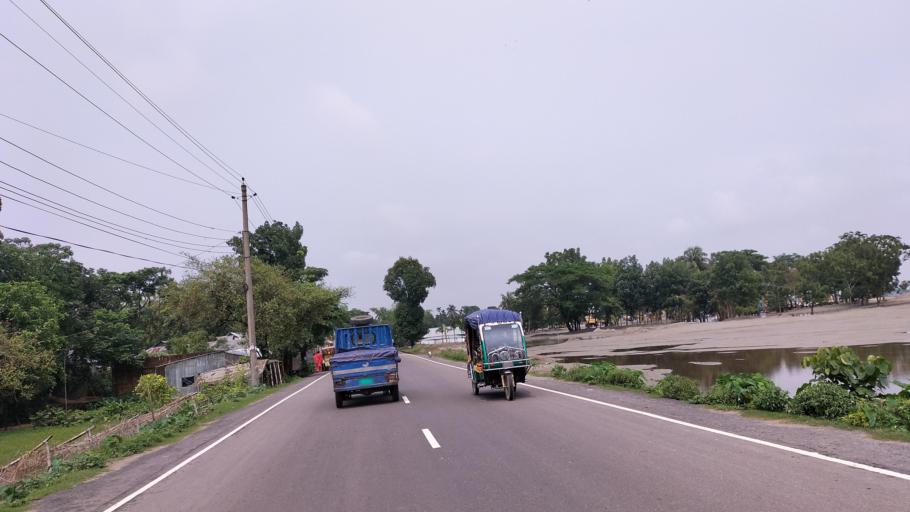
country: BD
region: Dhaka
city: Netrakona
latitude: 24.9014
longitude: 90.7558
